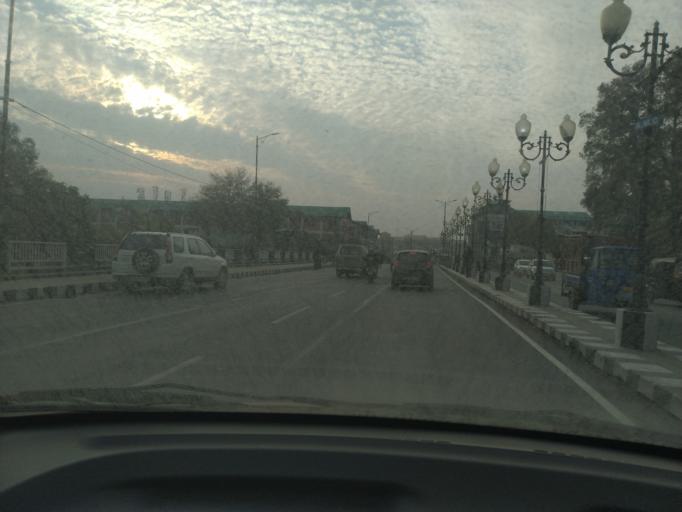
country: IN
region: Kashmir
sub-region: Srinagar
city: Srinagar
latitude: 34.0716
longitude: 74.8070
